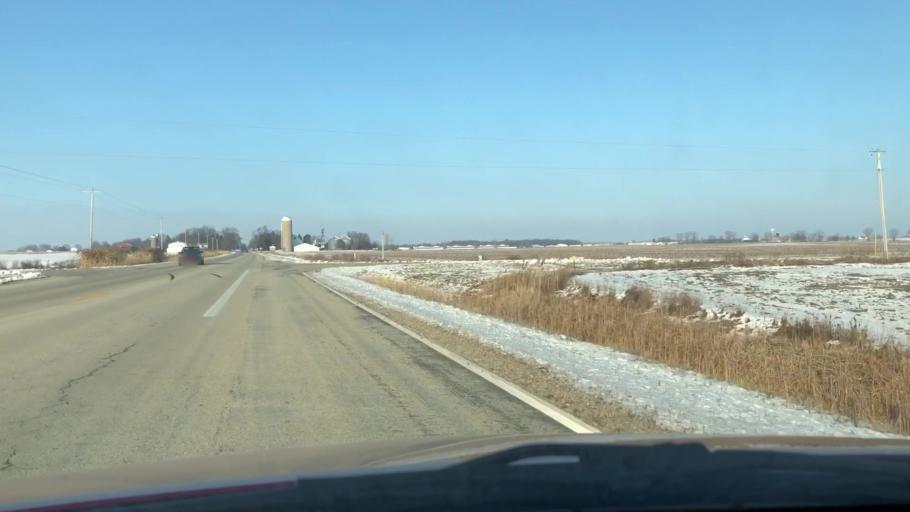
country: US
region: Wisconsin
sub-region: Outagamie County
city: Seymour
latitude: 44.4864
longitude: -88.3292
